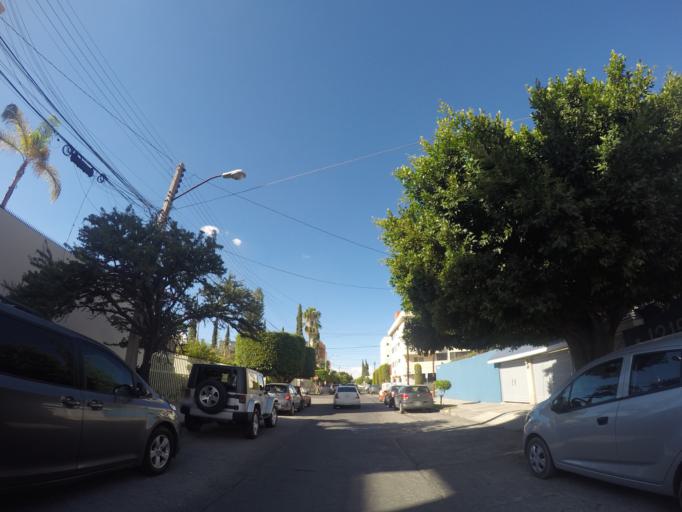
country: MX
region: San Luis Potosi
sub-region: San Luis Potosi
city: San Luis Potosi
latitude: 22.1411
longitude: -101.0046
